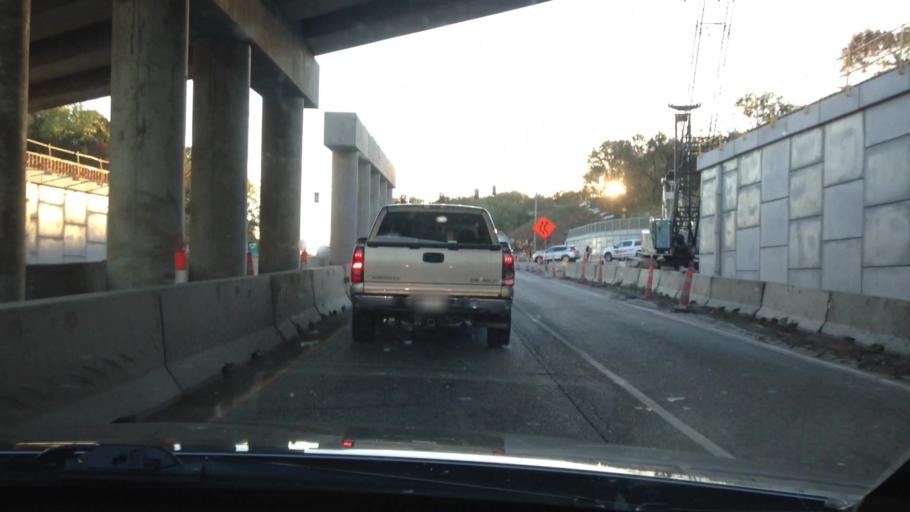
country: US
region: Missouri
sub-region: Clay County
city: Claycomo
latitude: 39.1591
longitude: -94.4973
